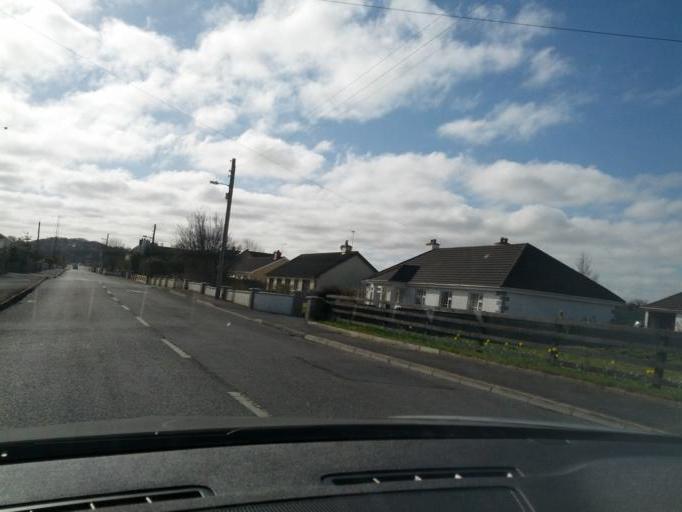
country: IE
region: Connaught
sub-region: County Galway
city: Ballinasloe
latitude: 53.3399
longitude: -8.2421
